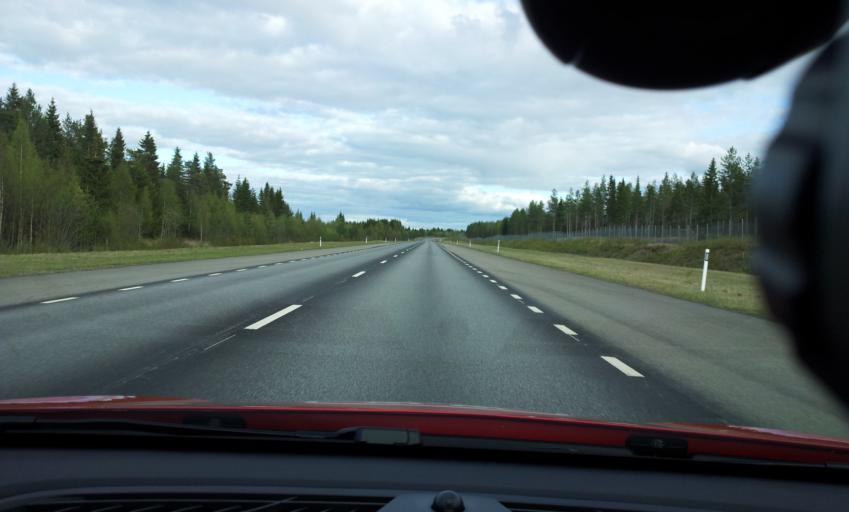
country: SE
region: Jaemtland
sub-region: OEstersunds Kommun
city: Ostersund
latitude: 63.1967
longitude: 14.5134
